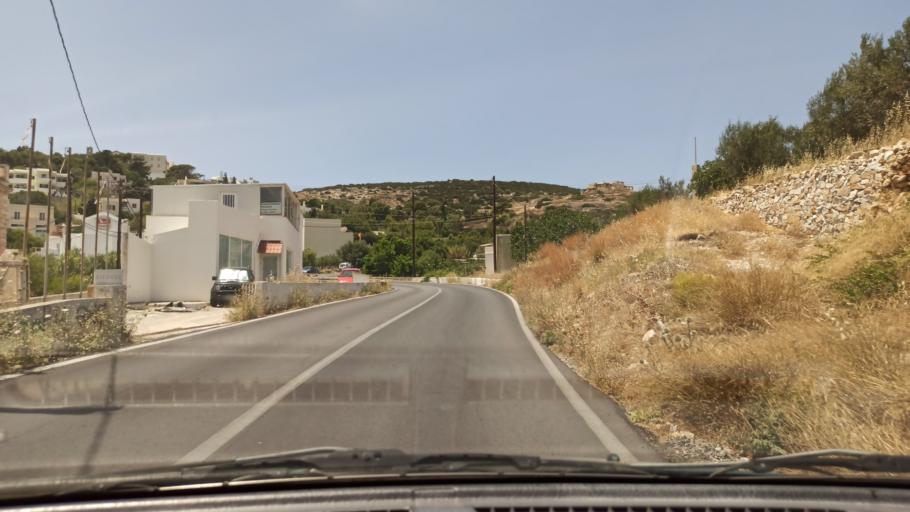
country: GR
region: South Aegean
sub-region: Nomos Kykladon
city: Ermoupolis
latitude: 37.4291
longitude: 24.9297
